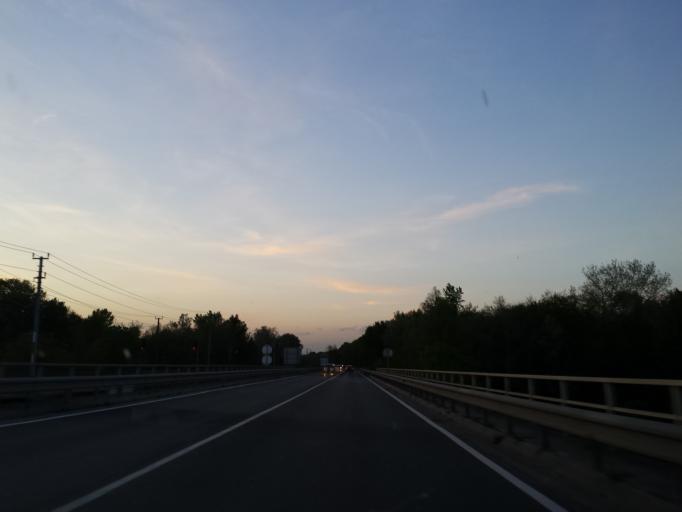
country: AT
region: Lower Austria
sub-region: Politischer Bezirk Tulln
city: Tulln
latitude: 48.3419
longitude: 16.0601
